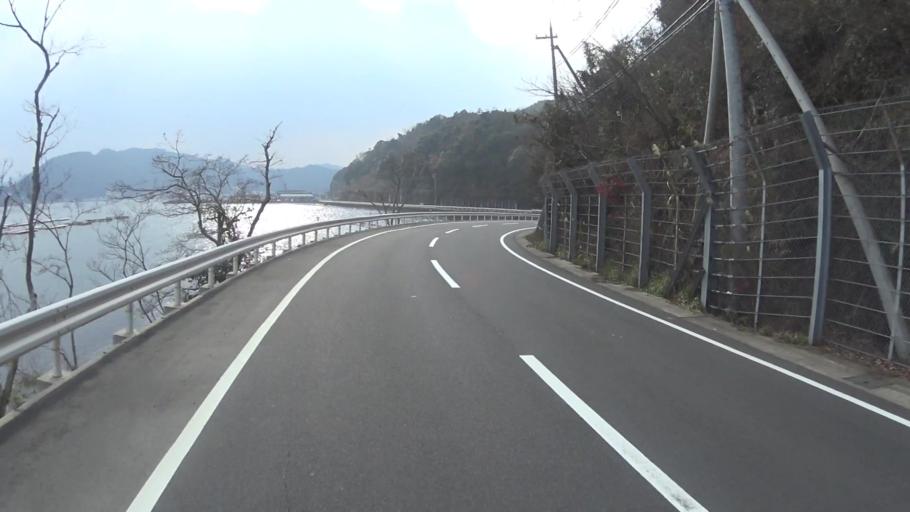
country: JP
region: Kyoto
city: Maizuru
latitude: 35.4680
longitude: 135.3189
